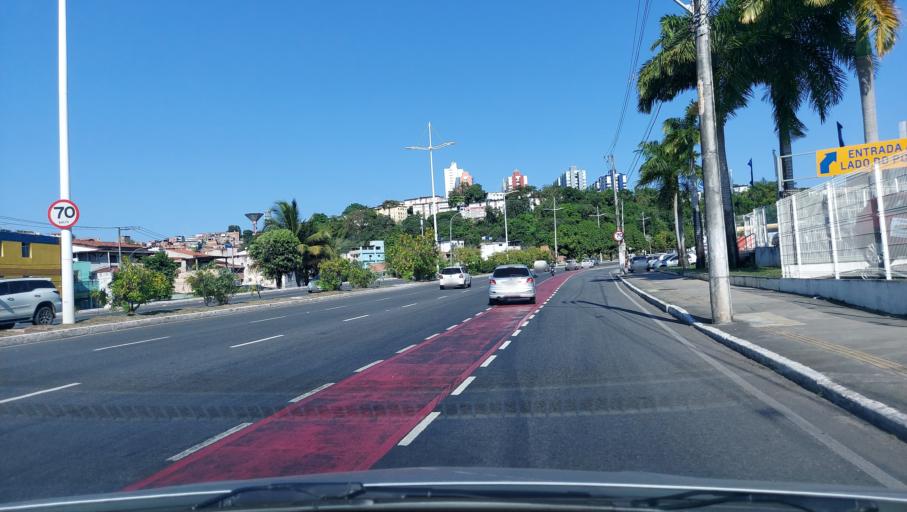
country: BR
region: Bahia
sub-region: Salvador
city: Salvador
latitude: -12.9547
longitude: -38.4703
